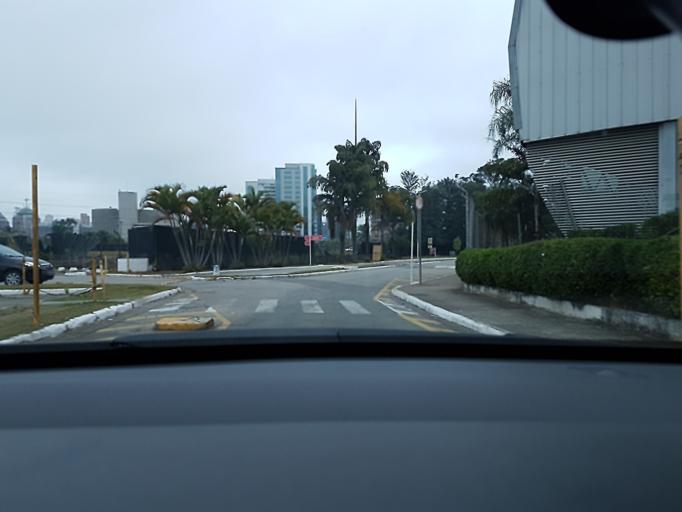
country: BR
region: Sao Paulo
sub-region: Taboao Da Serra
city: Taboao da Serra
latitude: -23.6283
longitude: -46.7171
